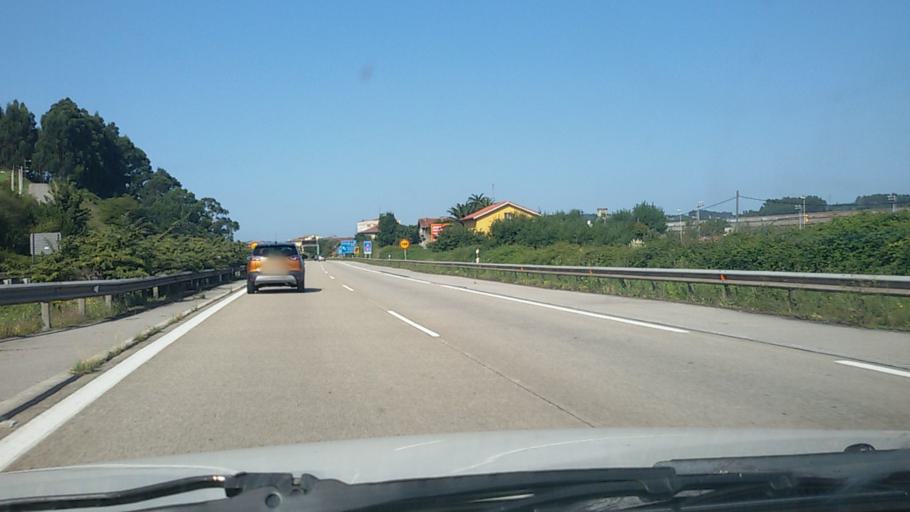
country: ES
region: Asturias
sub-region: Province of Asturias
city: Corvera de Asturias
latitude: 43.5515
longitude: -5.8808
